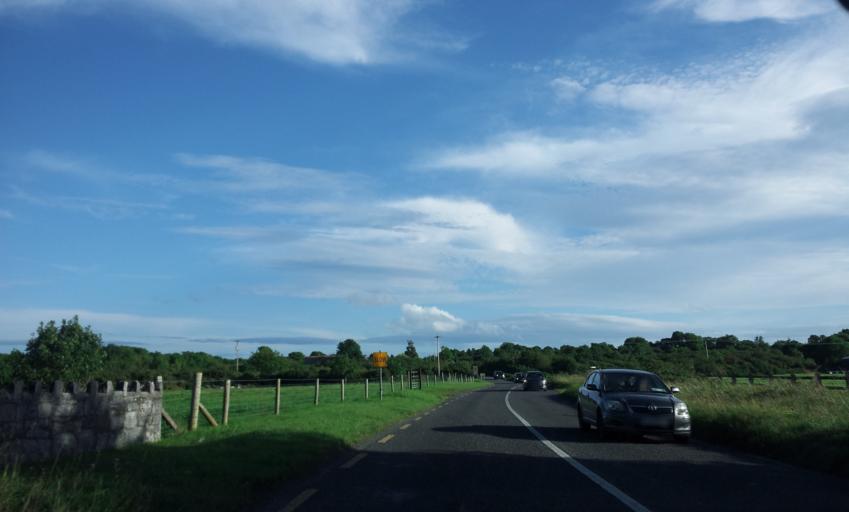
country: IE
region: Munster
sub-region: An Clar
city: Ennis
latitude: 52.9203
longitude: -9.0470
